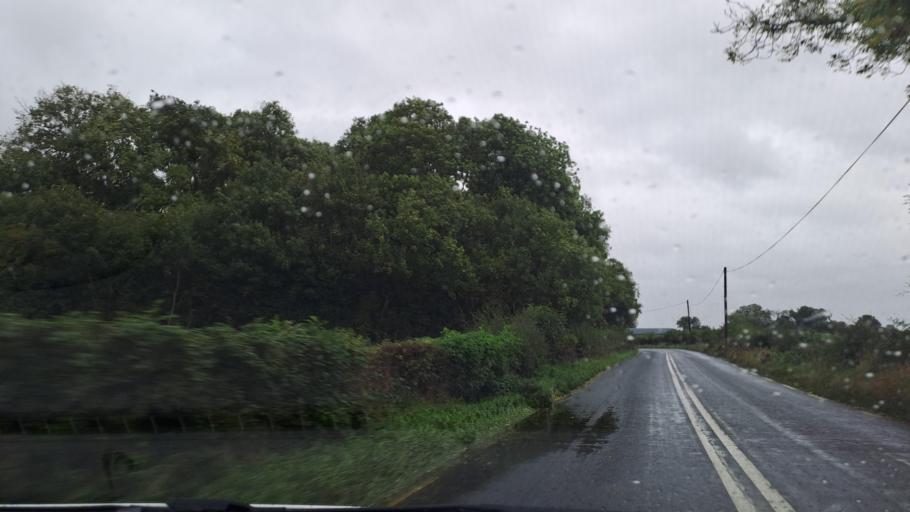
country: IE
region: Leinster
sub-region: Lu
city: Dundalk
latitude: 53.9784
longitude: -6.5166
